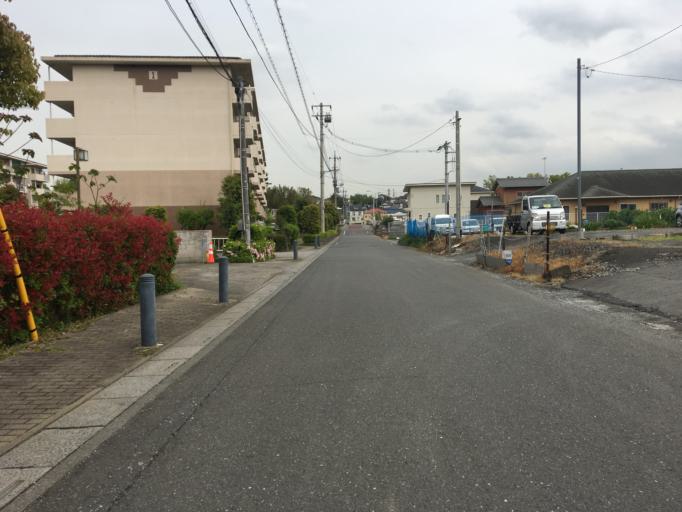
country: JP
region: Saitama
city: Oi
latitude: 35.8491
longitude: 139.5497
